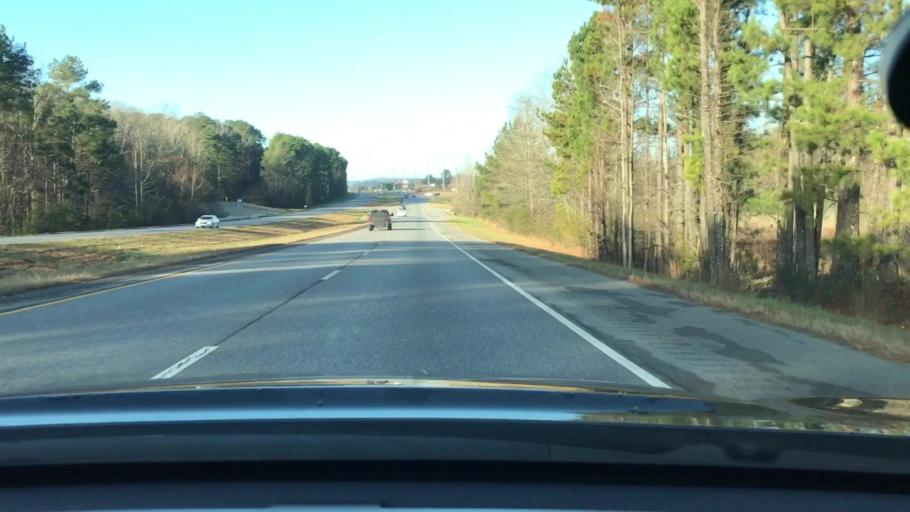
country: US
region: Alabama
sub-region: Shelby County
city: Chelsea
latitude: 33.3511
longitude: -86.6027
